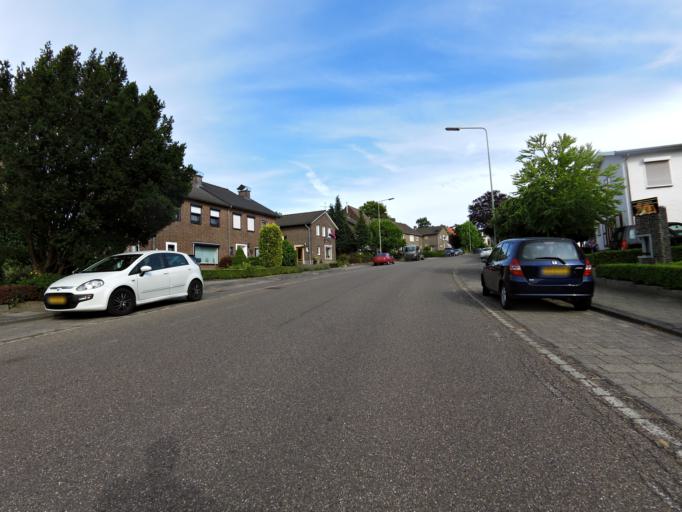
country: NL
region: Limburg
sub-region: Gemeente Heerlen
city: Heerlen
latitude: 50.9011
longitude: 6.0111
